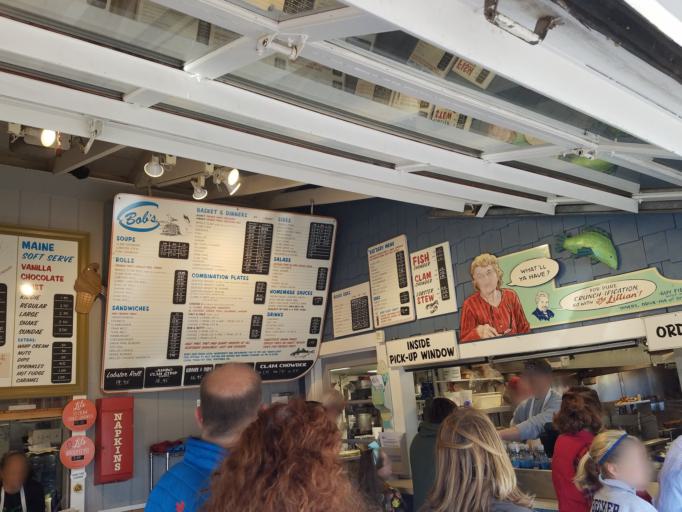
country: US
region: Maine
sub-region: York County
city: Kittery
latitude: 43.1121
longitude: -70.7340
